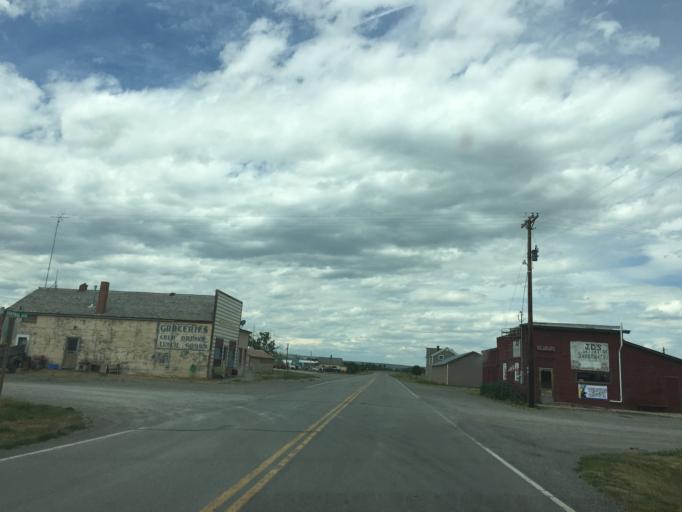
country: US
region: Montana
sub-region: Teton County
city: Choteau
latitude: 47.9775
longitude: -112.3118
